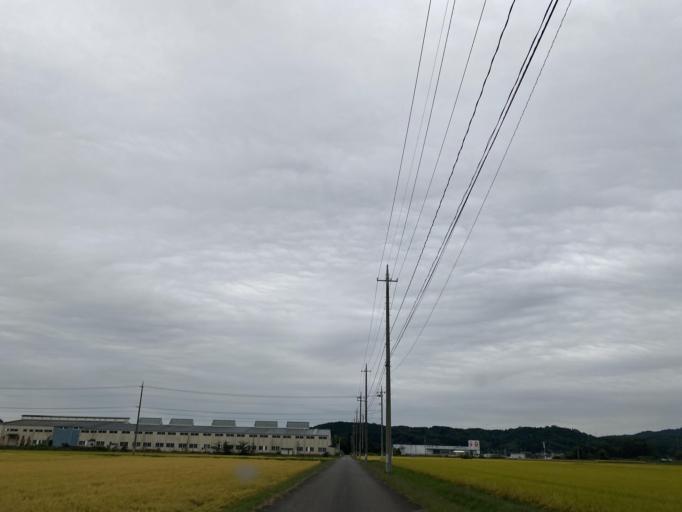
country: JP
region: Fukushima
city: Sukagawa
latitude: 37.2867
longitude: 140.2515
